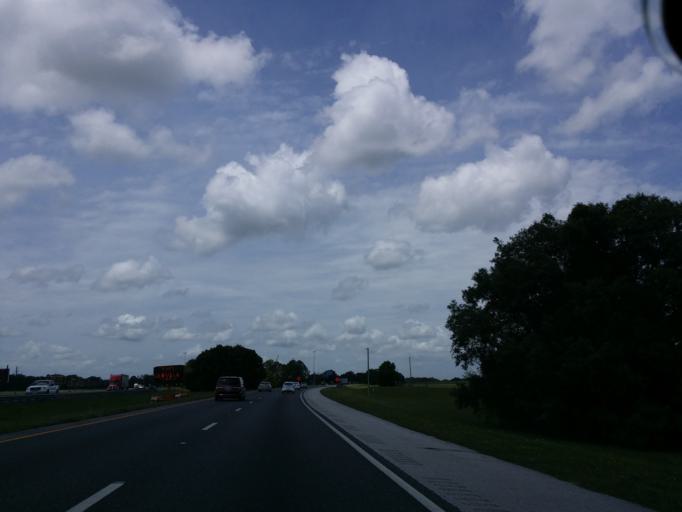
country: US
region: Florida
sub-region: Lake County
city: Leesburg
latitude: 28.7827
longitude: -81.9745
